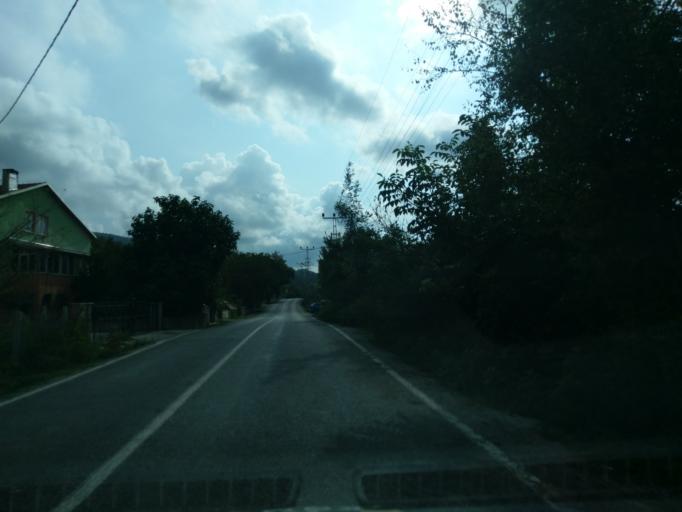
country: TR
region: Sinop
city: Helaldi
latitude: 41.9092
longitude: 34.4336
